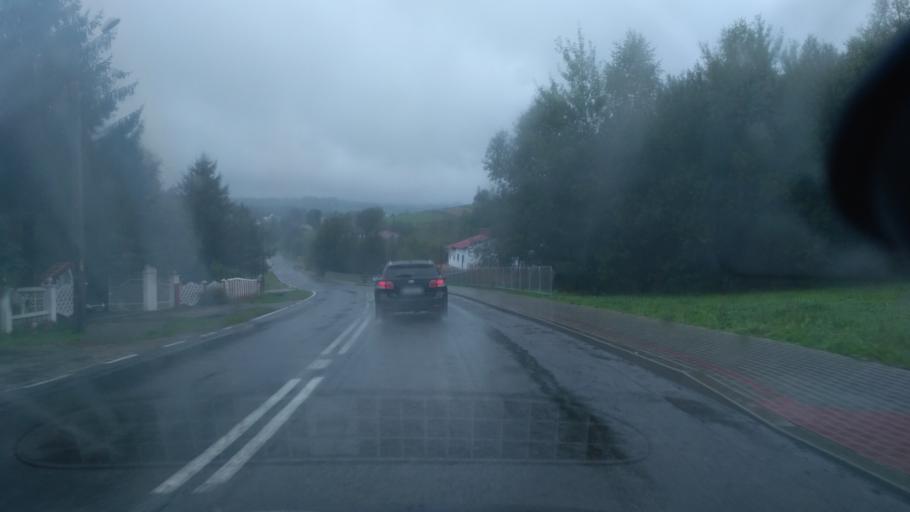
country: PL
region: Subcarpathian Voivodeship
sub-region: Powiat ropczycko-sedziszowski
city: Niedzwiada
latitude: 50.0027
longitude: 21.5599
